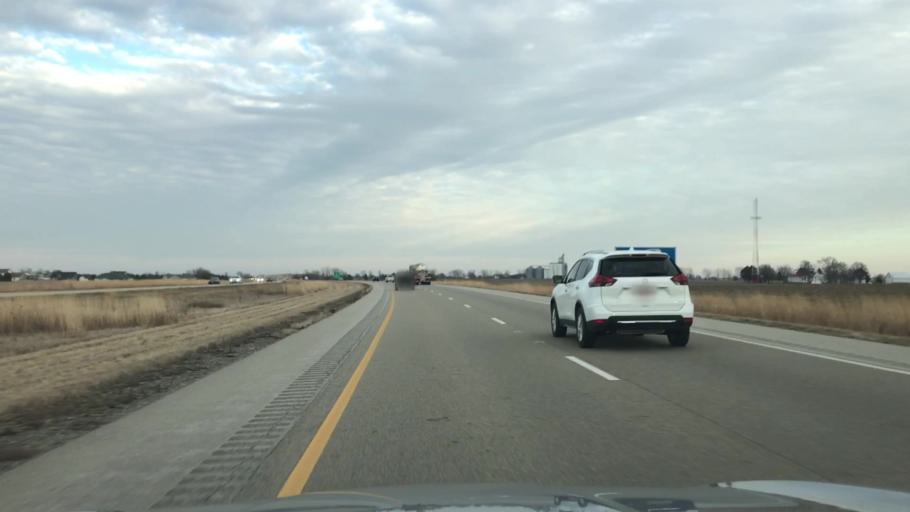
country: US
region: Illinois
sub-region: Logan County
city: Lincoln
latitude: 40.1817
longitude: -89.3461
